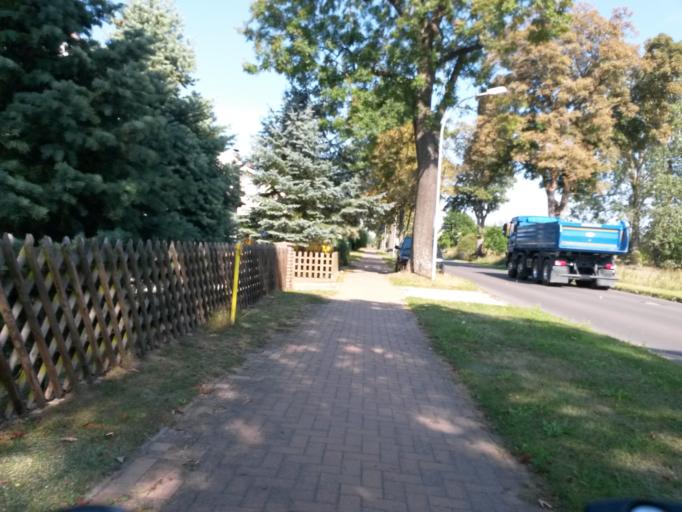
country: DE
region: Brandenburg
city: Templin
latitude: 53.0974
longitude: 13.4652
